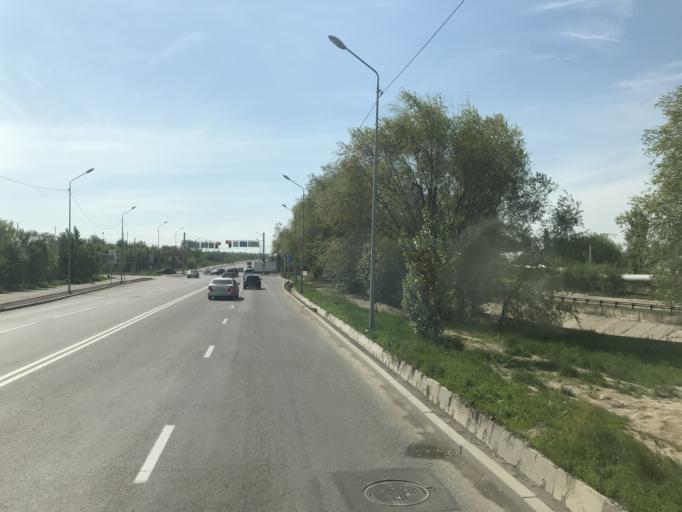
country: KZ
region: Almaty Oblysy
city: Burunday
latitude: 43.3130
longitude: 76.8503
